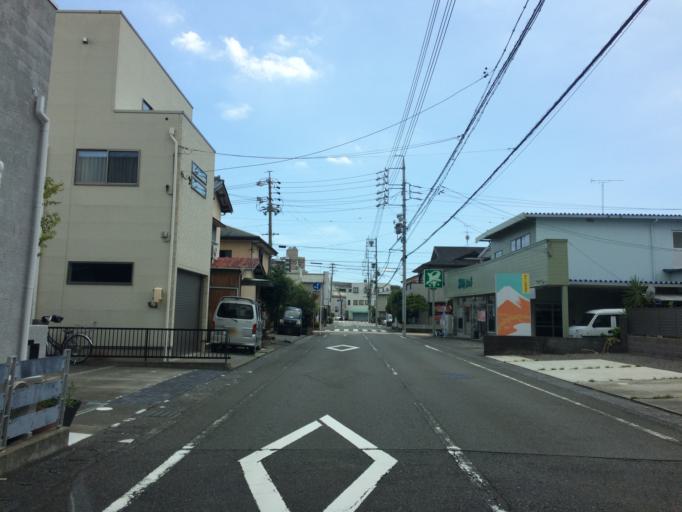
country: JP
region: Shizuoka
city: Yaizu
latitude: 34.8751
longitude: 138.3152
